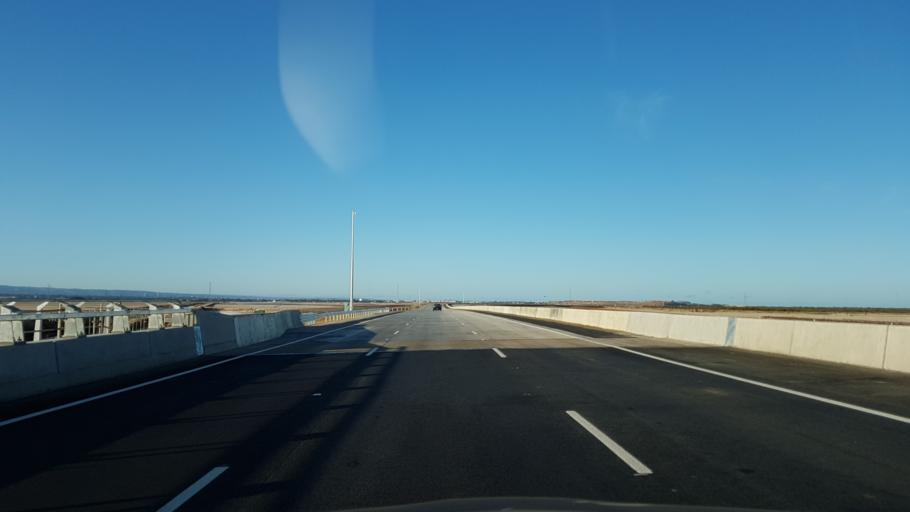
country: AU
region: South Australia
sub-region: Salisbury
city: Salisbury
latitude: -34.7951
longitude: 138.5783
